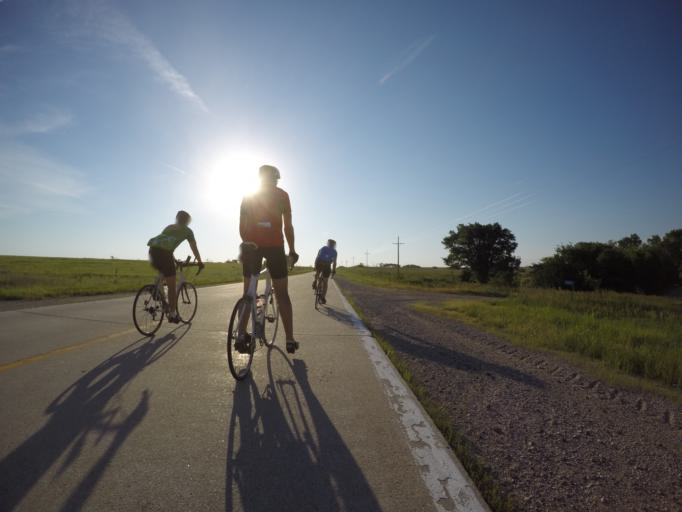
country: US
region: Nebraska
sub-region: Gage County
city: Wymore
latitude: 40.0448
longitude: -96.6030
